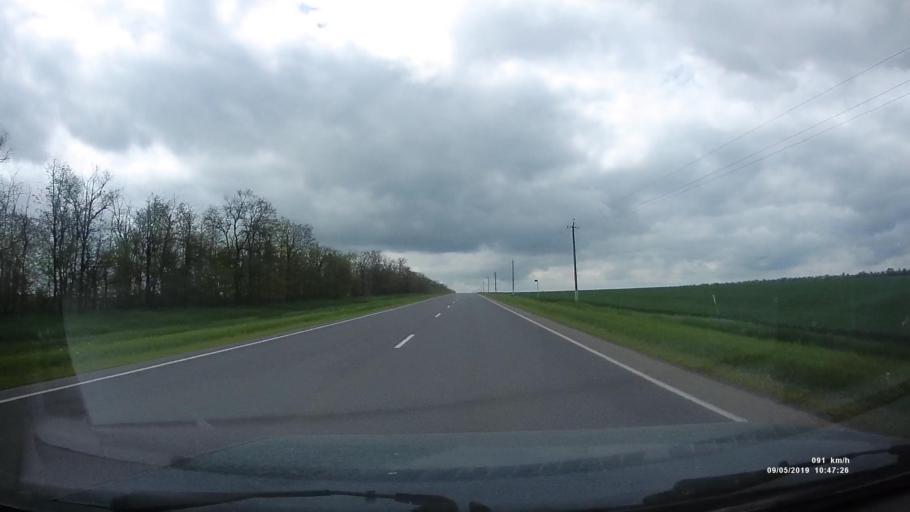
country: RU
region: Rostov
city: Peshkovo
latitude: 46.9707
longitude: 39.3556
